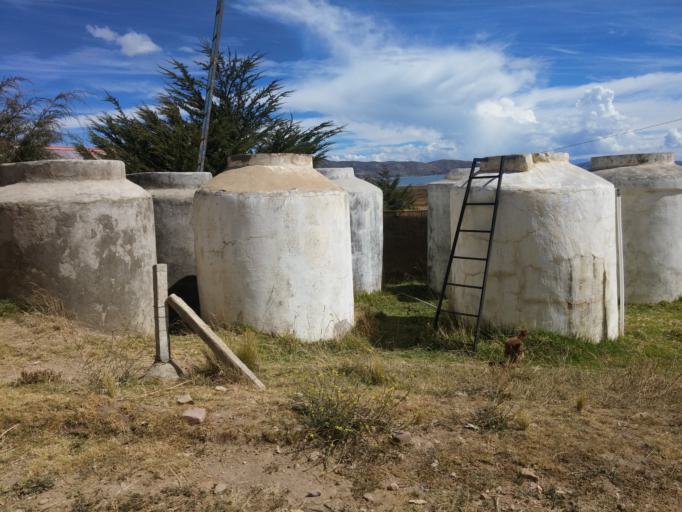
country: BO
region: La Paz
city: Batallas
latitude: -16.2922
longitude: -68.6012
